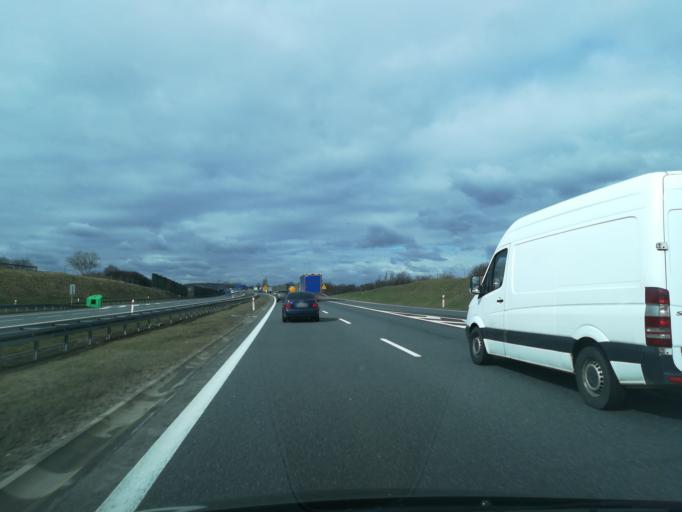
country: PL
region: Lesser Poland Voivodeship
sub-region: Powiat chrzanowski
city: Chrzanow
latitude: 50.1490
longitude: 19.4247
